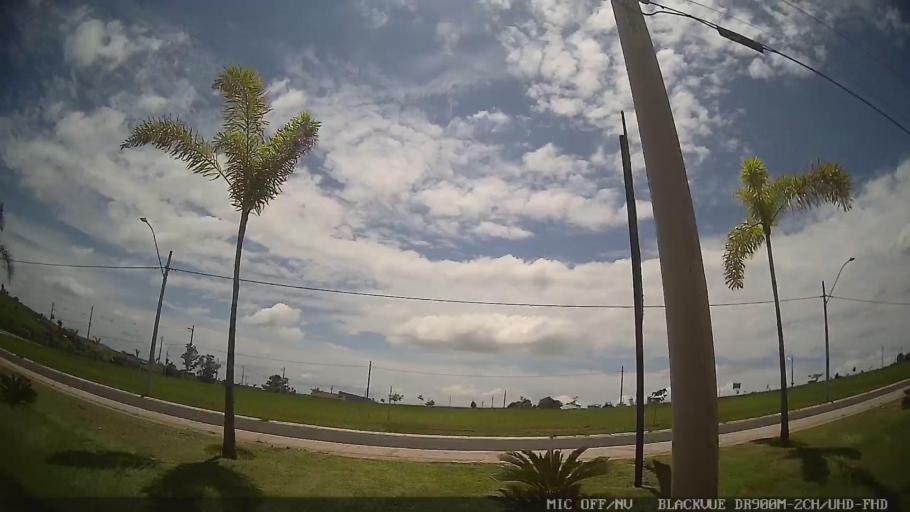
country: BR
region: Sao Paulo
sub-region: Laranjal Paulista
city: Laranjal Paulista
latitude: -23.0306
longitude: -47.8386
